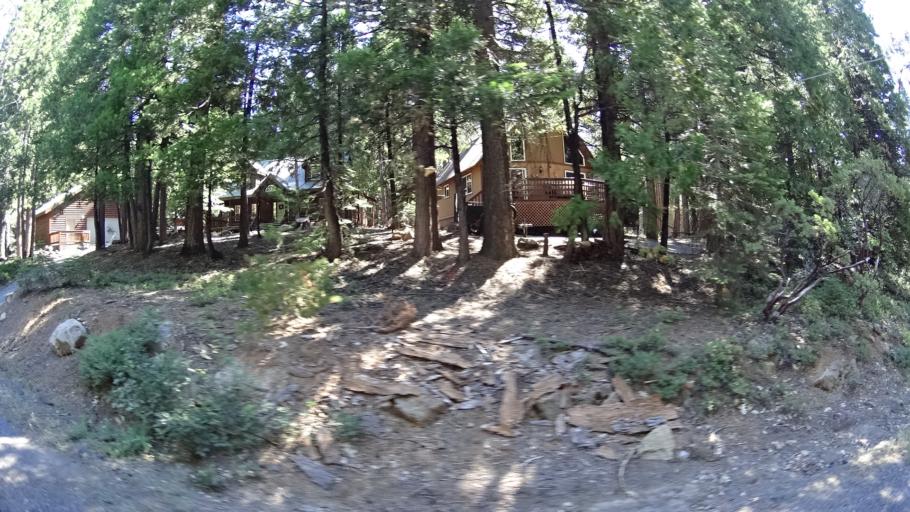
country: US
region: California
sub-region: Calaveras County
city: Arnold
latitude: 38.2965
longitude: -120.2704
